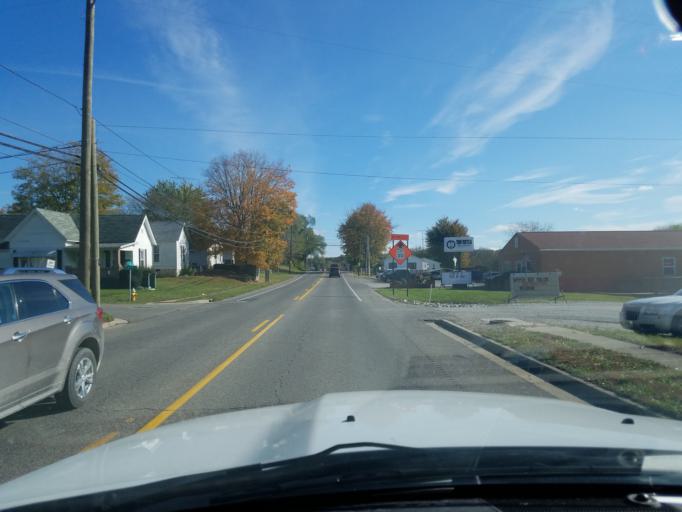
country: US
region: Indiana
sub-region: Jennings County
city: North Vernon
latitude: 39.0057
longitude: -85.6174
